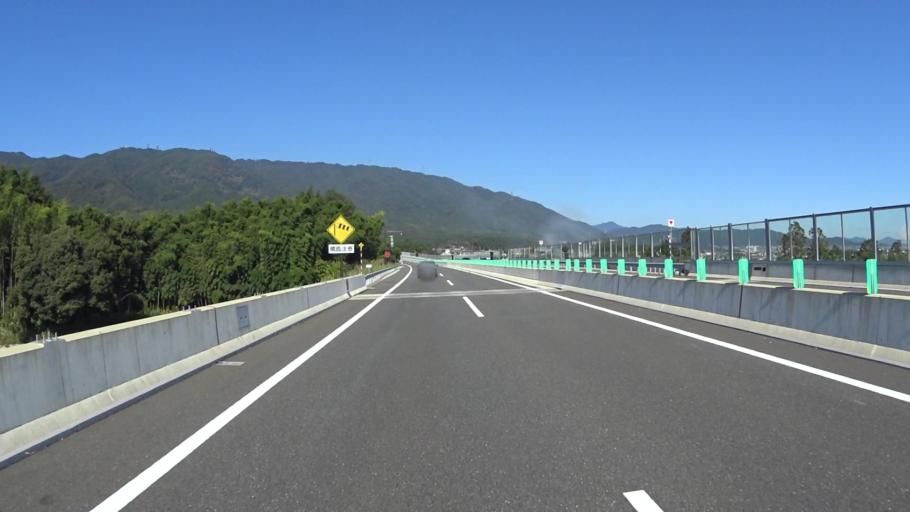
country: JP
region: Kyoto
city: Muko
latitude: 34.9501
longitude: 135.6622
